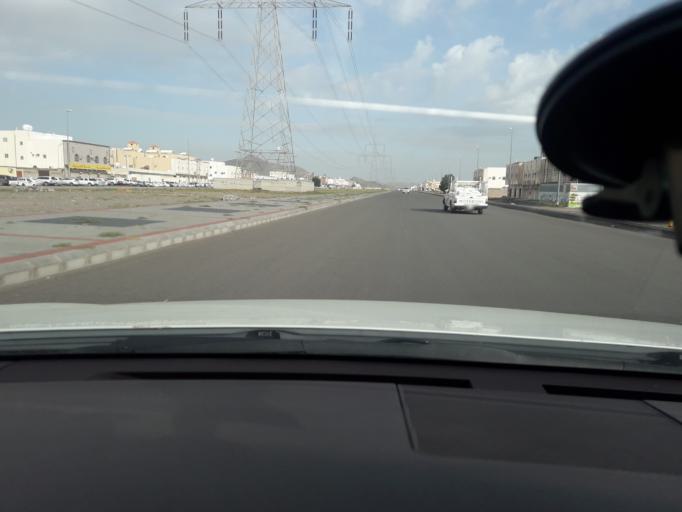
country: SA
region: Al Madinah al Munawwarah
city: Sultanah
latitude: 24.4375
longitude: 39.4930
